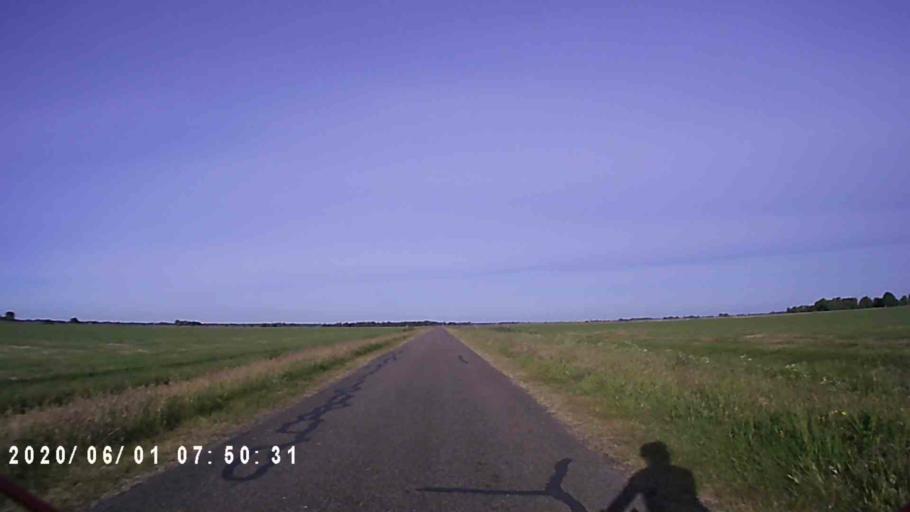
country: NL
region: Friesland
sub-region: Gemeente Dantumadiel
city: Rinsumageast
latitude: 53.2890
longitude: 5.9516
